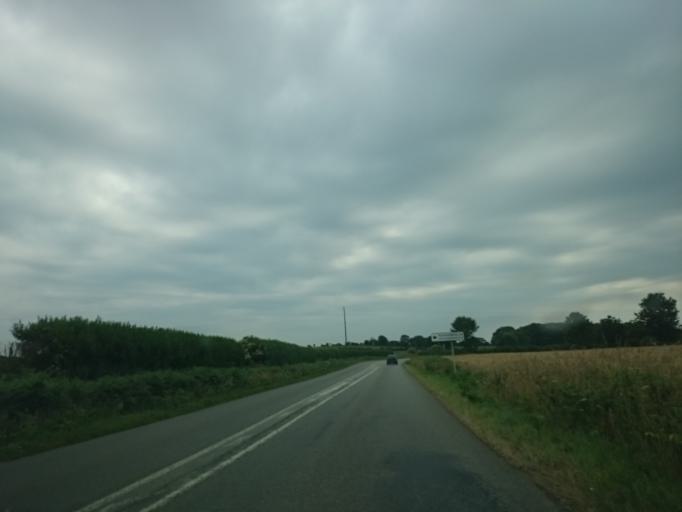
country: FR
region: Brittany
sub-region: Departement du Finistere
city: Ploumoguer
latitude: 48.3989
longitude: -4.6687
